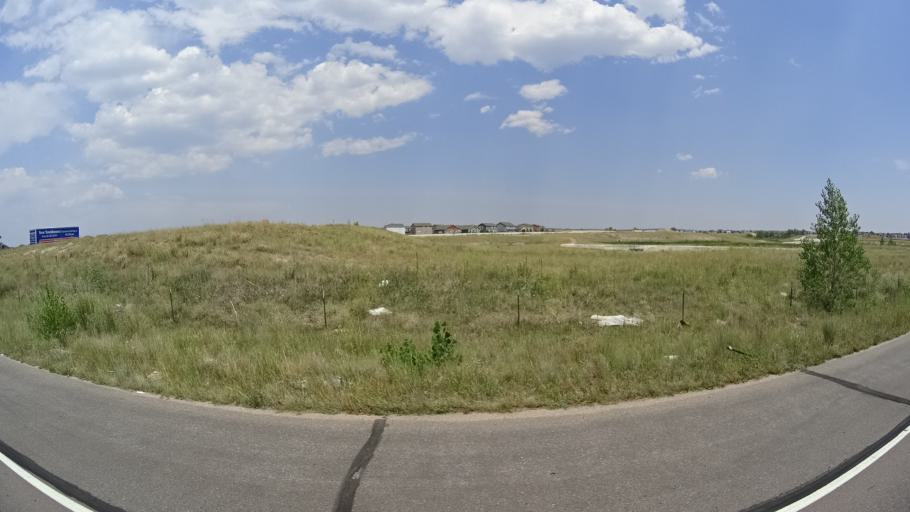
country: US
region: Colorado
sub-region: El Paso County
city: Black Forest
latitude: 38.9415
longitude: -104.6839
